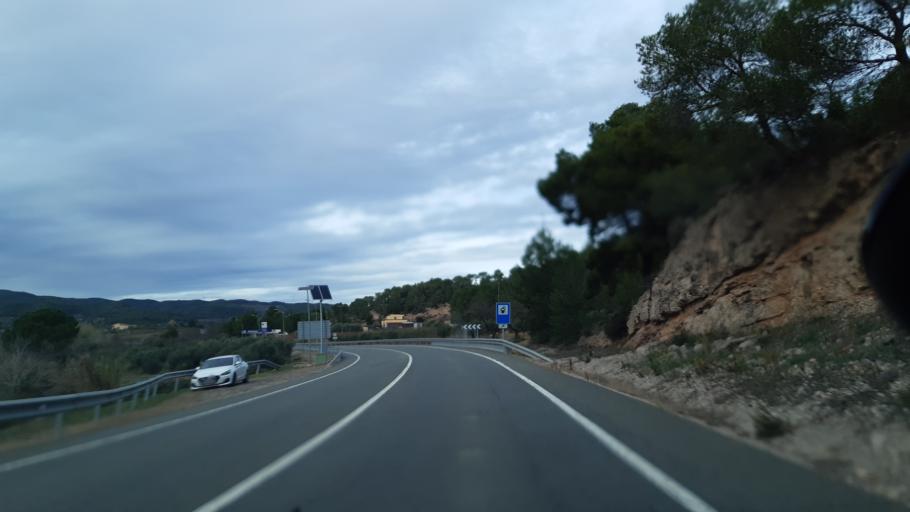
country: ES
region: Catalonia
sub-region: Provincia de Tarragona
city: la Fatarella
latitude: 41.1064
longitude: 0.5383
